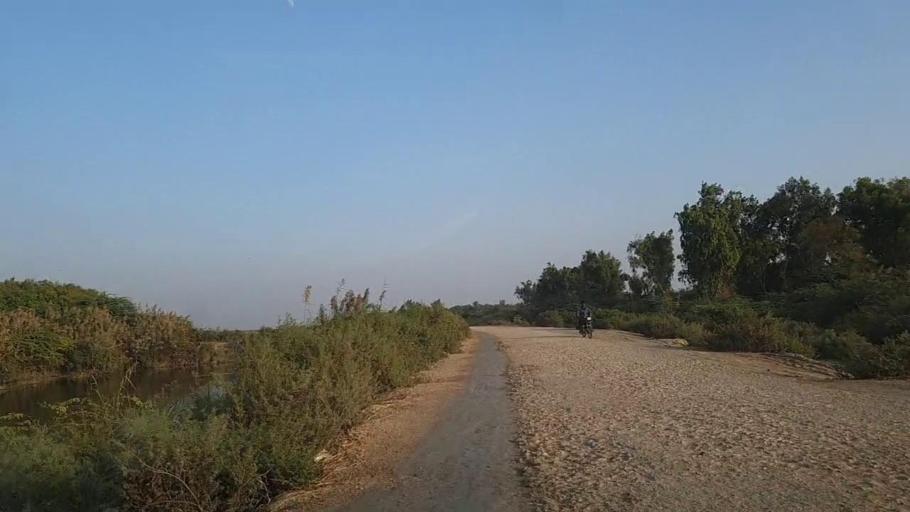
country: PK
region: Sindh
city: Keti Bandar
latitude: 24.2721
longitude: 67.6769
